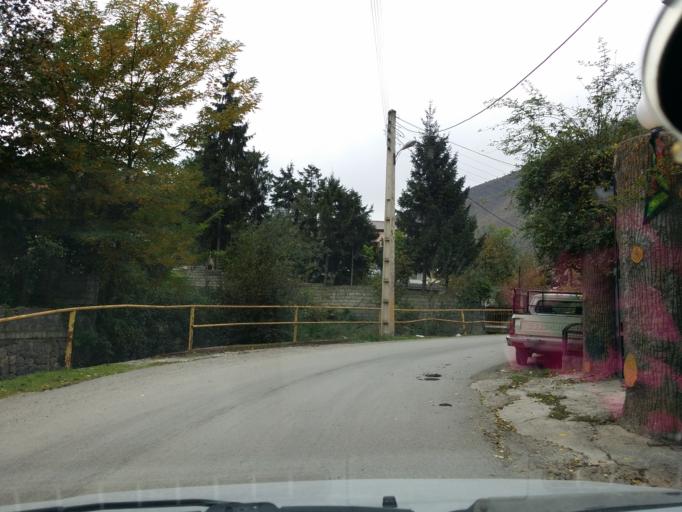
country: IR
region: Mazandaran
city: `Abbasabad
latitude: 36.5005
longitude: 51.1469
